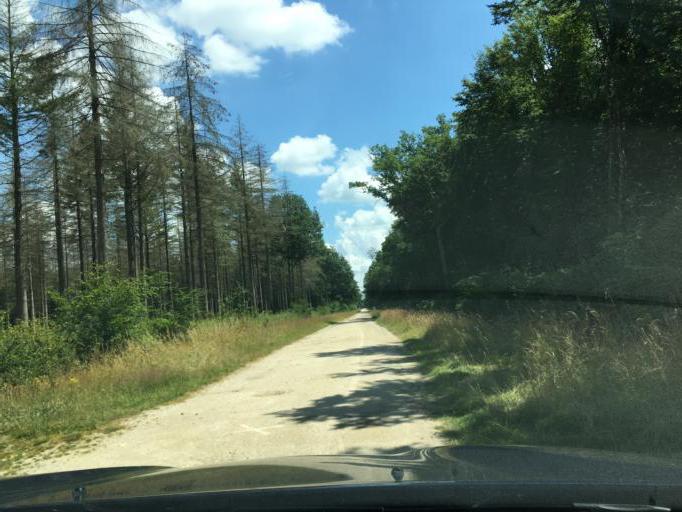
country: FR
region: Centre
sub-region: Departement du Loiret
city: Saran
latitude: 47.9830
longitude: 1.8936
